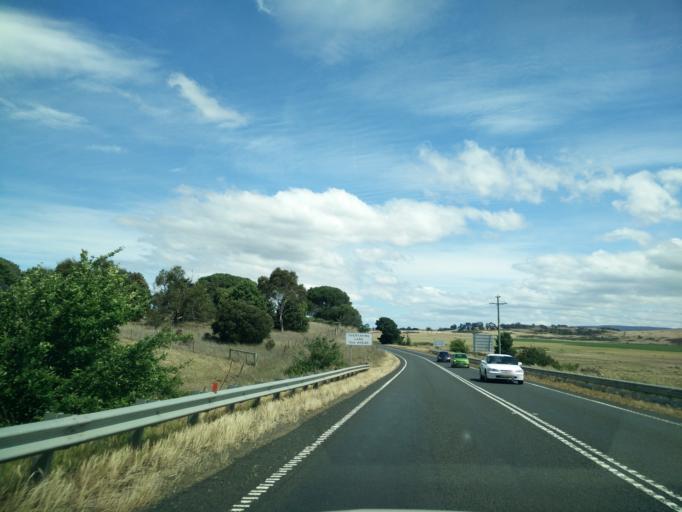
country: AU
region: Tasmania
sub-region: Northern Midlands
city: Evandale
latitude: -41.8423
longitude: 147.4481
